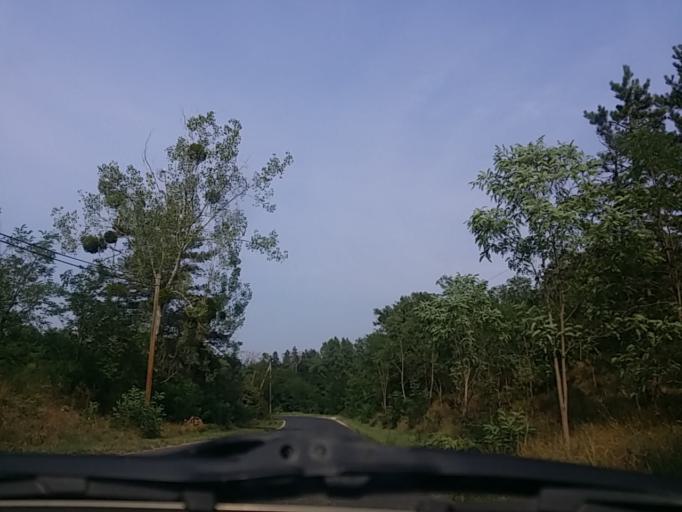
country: HU
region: Komarom-Esztergom
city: Kornye
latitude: 47.5235
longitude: 18.3692
